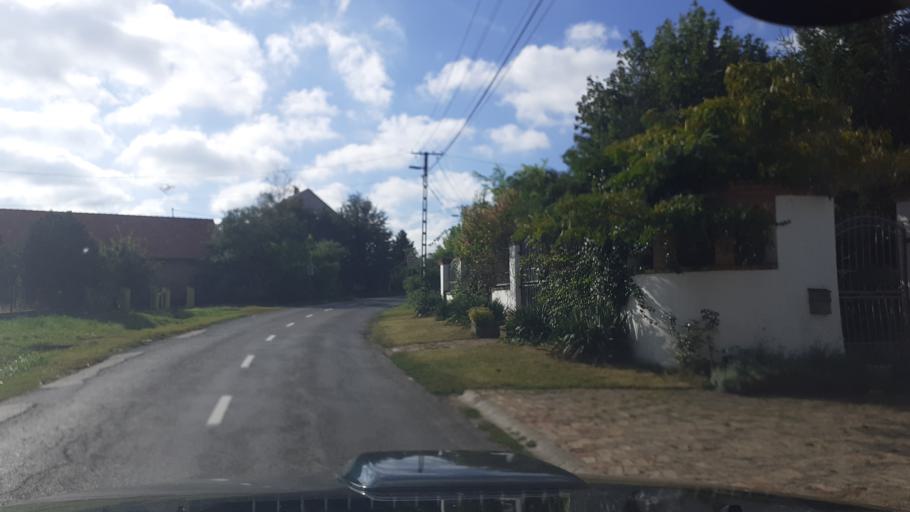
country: HU
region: Fejer
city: Baracs
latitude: 46.8973
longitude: 18.8980
